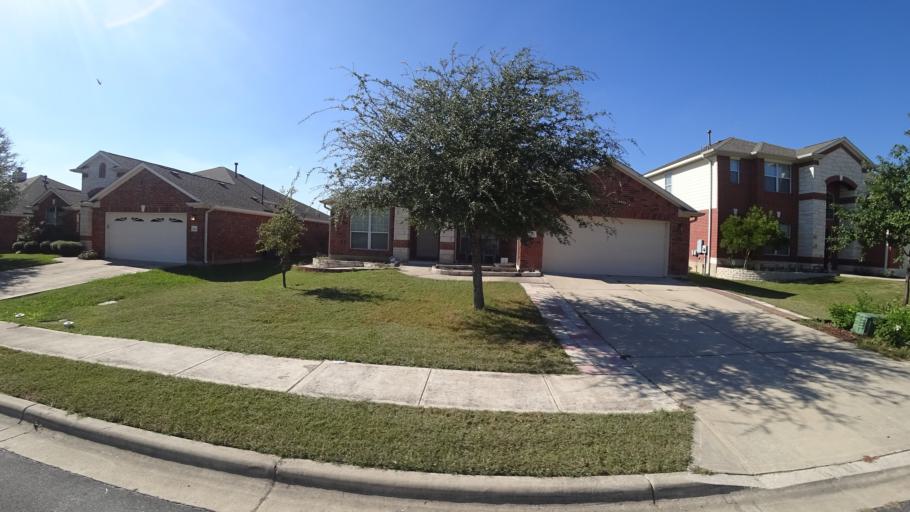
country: US
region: Texas
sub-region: Travis County
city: Manor
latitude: 30.3564
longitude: -97.6084
